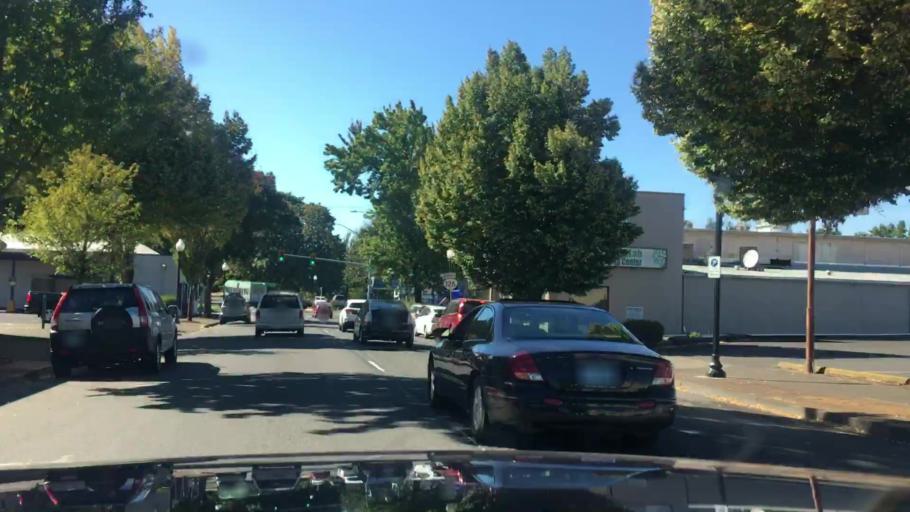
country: US
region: Oregon
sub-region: Lane County
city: Springfield
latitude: 44.0462
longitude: -123.0235
